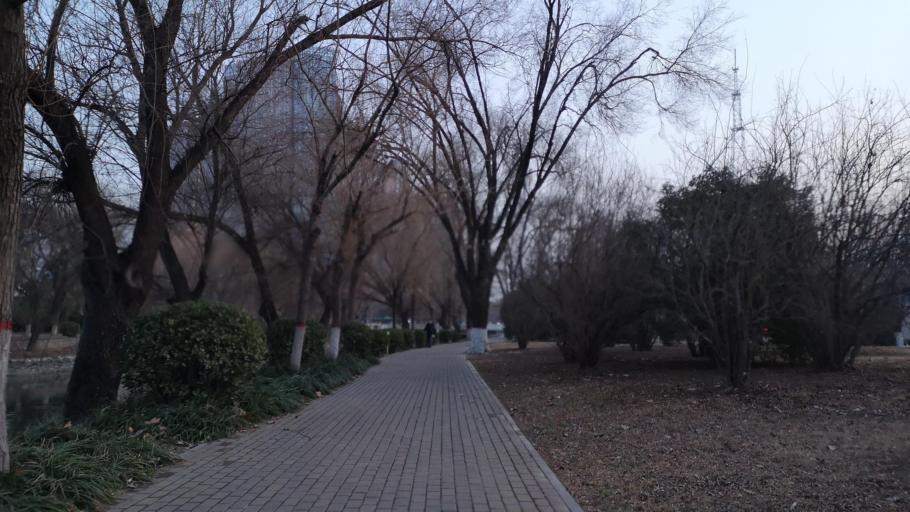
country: CN
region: Henan Sheng
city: Zhongyuanlu
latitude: 35.7769
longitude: 115.0778
